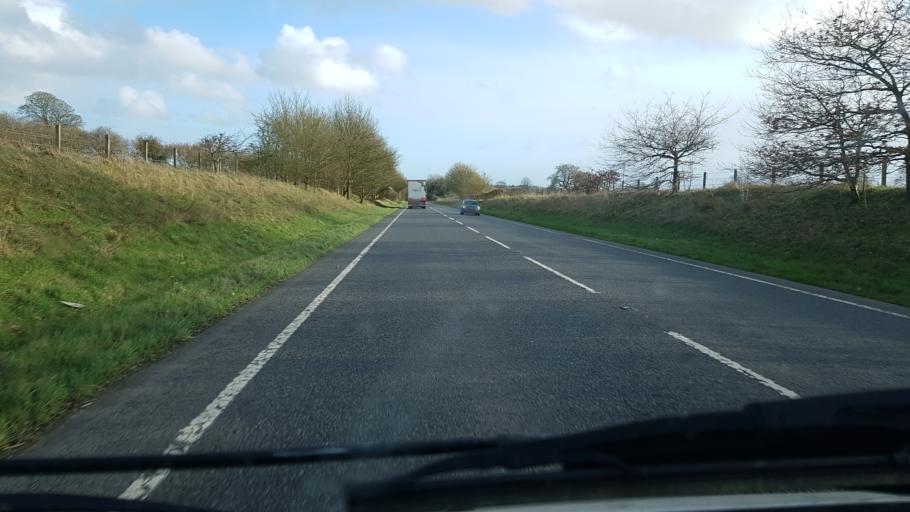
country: GB
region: England
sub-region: Wiltshire
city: Burbage
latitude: 51.3508
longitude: -1.6752
